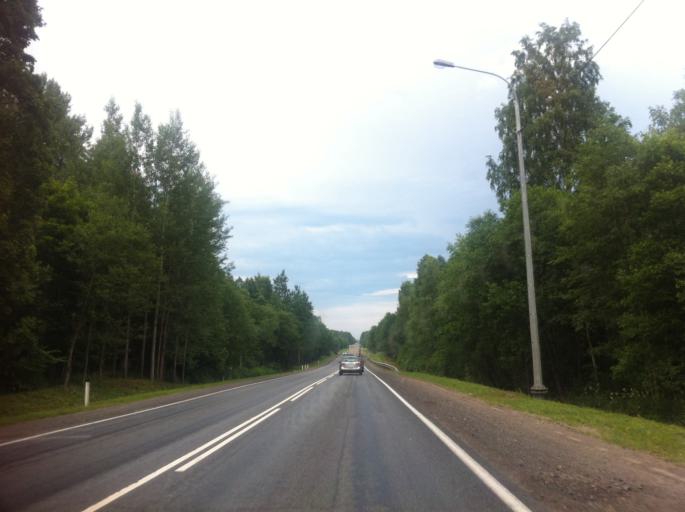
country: RU
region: Pskov
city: Strugi-Krasnyye
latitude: 58.1069
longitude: 29.0965
